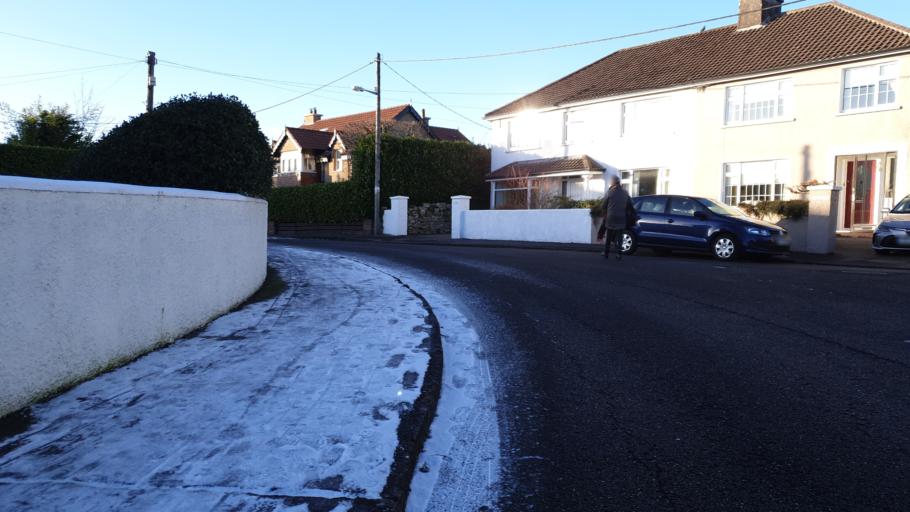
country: IE
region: Munster
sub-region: County Cork
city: Cork
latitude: 51.8924
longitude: -8.4431
